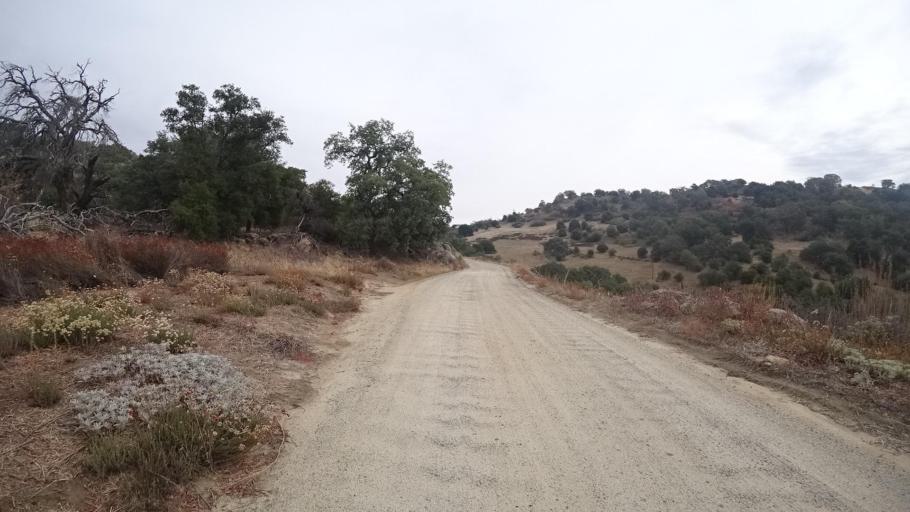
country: US
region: California
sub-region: San Diego County
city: Julian
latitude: 33.0300
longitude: -116.6608
